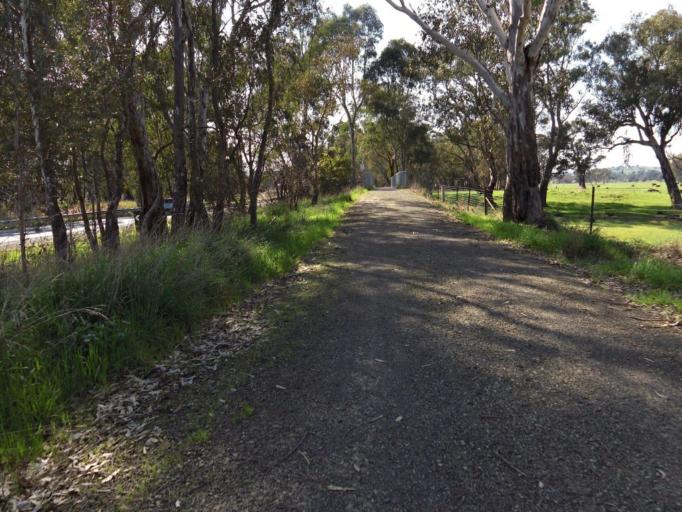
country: AU
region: Victoria
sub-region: Murrindindi
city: Alexandra
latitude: -37.1519
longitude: 145.5794
